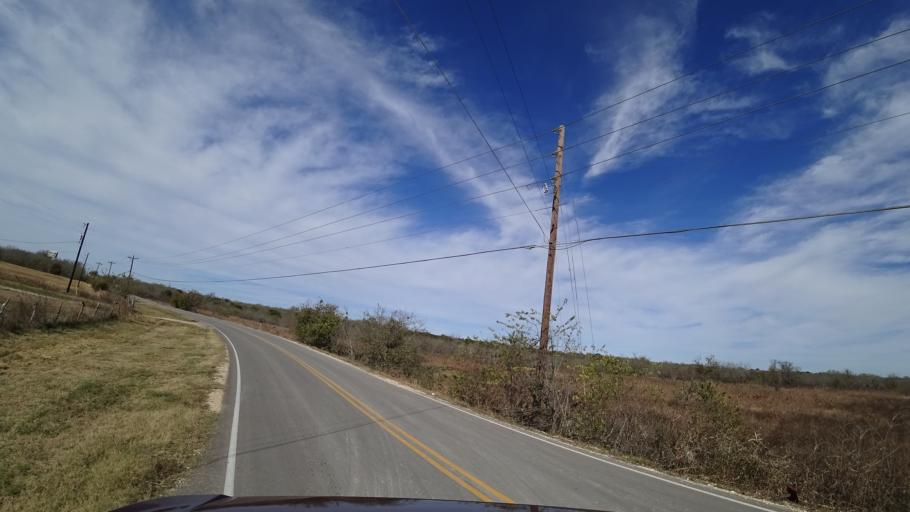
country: US
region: Texas
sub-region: Travis County
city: Onion Creek
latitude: 30.1052
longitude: -97.6908
